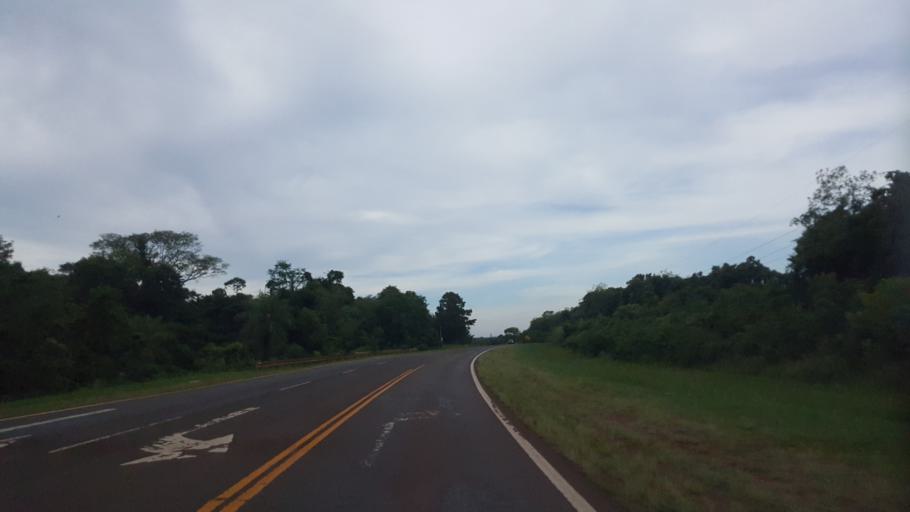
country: AR
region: Misiones
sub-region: Departamento de Candelaria
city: Loreto
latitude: -27.3329
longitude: -55.5434
